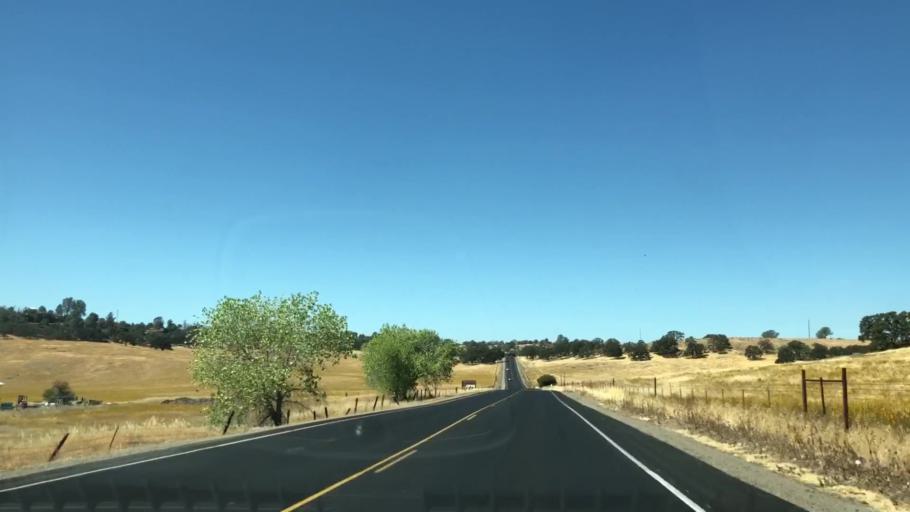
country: US
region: California
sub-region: Tuolumne County
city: Jamestown
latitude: 37.8800
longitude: -120.4660
